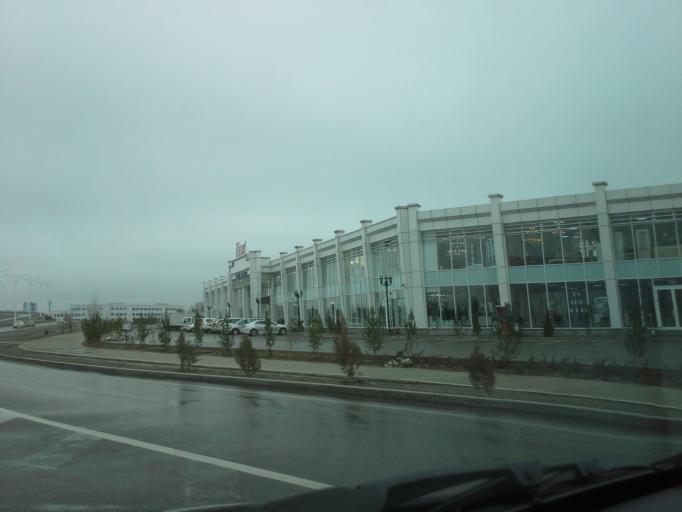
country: TM
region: Ahal
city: Ashgabat
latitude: 37.9620
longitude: 58.4159
